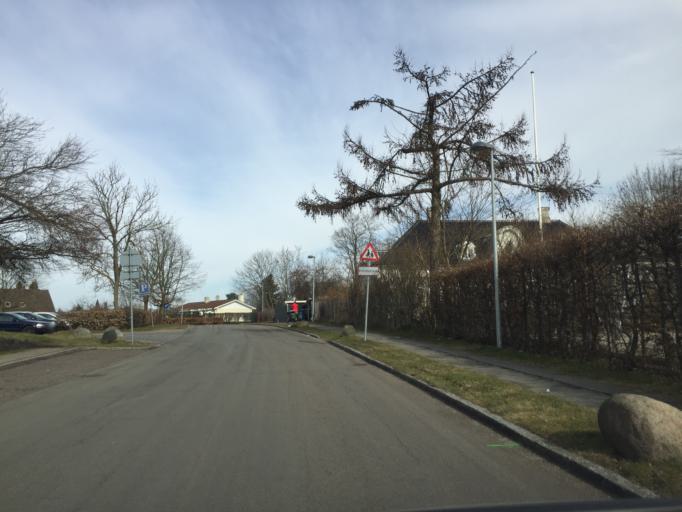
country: DK
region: Capital Region
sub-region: Fureso Kommune
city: Farum
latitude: 55.8086
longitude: 12.3590
